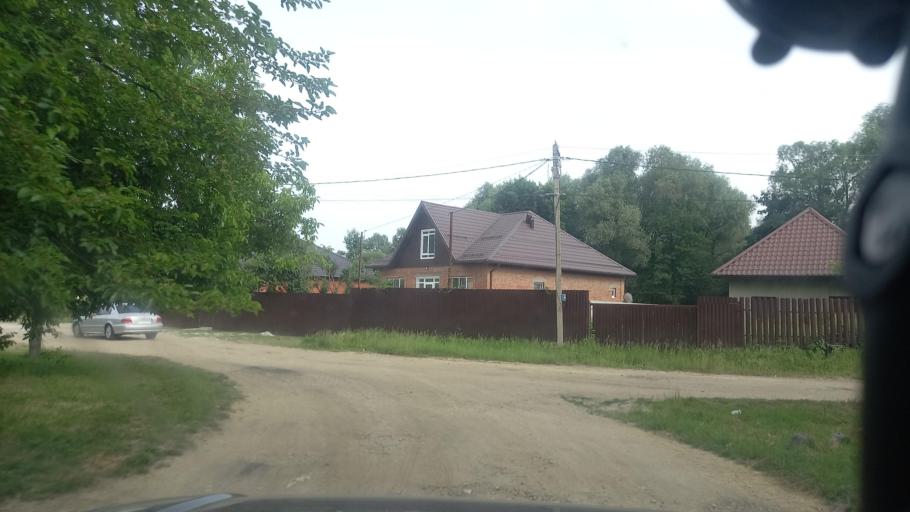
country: RU
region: Krasnodarskiy
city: Goryachiy Klyuch
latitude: 44.6040
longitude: 39.0317
